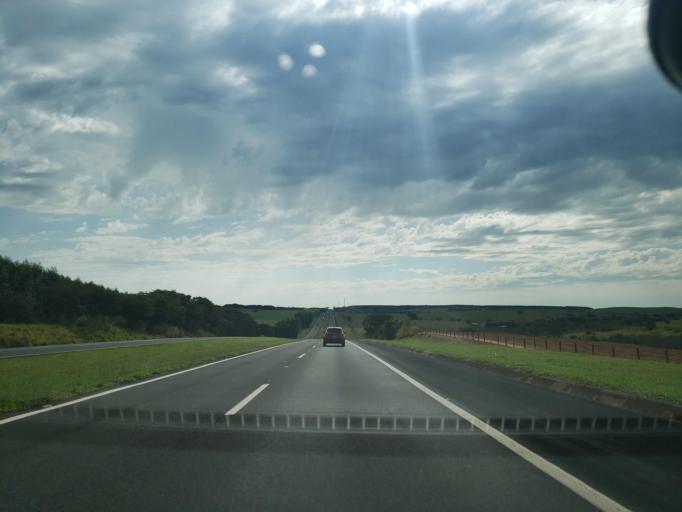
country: BR
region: Sao Paulo
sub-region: Cafelandia
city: Cafelandia
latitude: -21.7870
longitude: -49.6534
